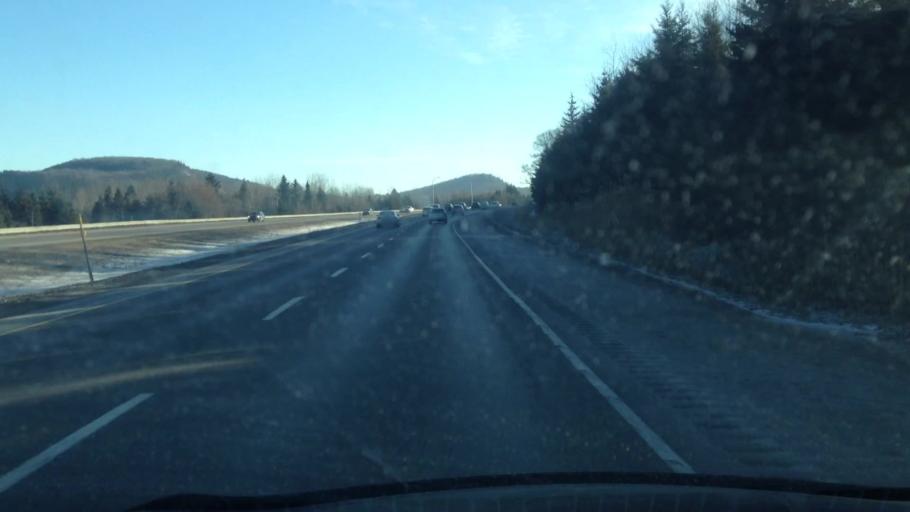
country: CA
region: Quebec
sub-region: Laurentides
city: Prevost
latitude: 45.8851
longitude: -74.1116
